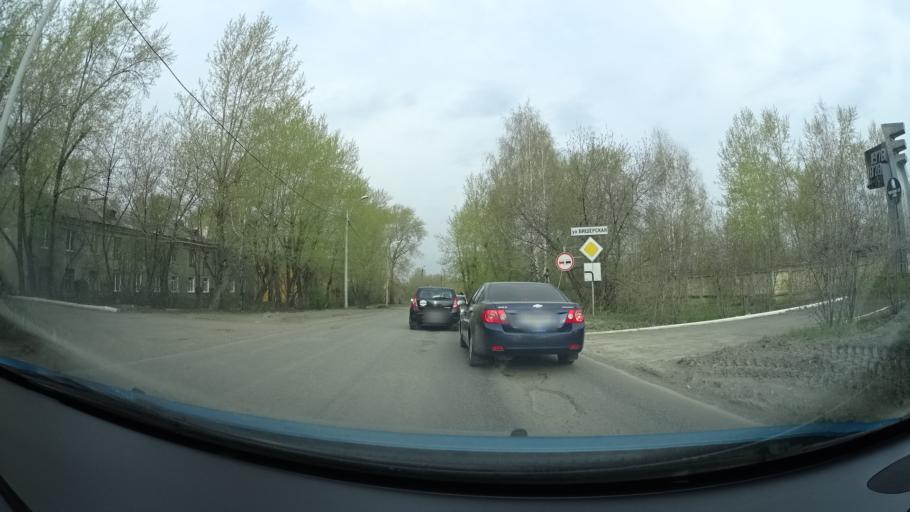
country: RU
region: Perm
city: Kondratovo
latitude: 58.0025
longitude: 56.1657
